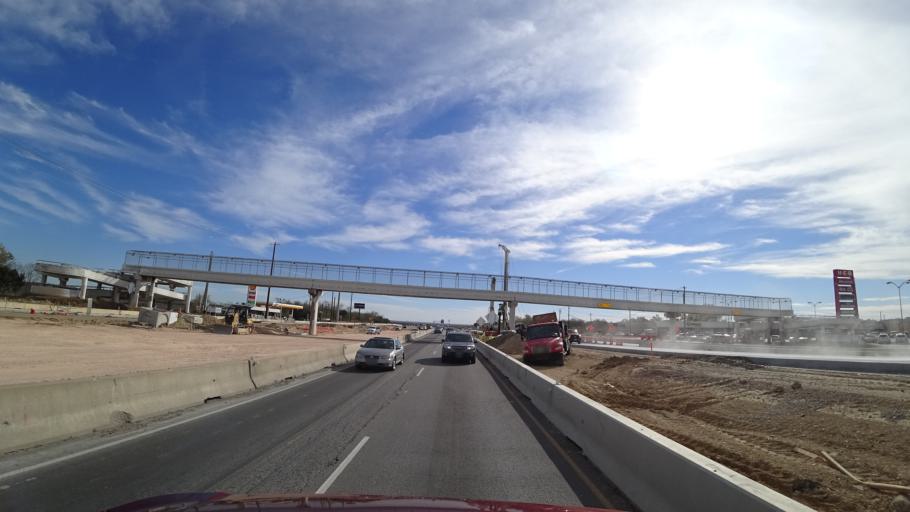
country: US
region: Texas
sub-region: Travis County
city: Austin
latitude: 30.3132
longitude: -97.6624
